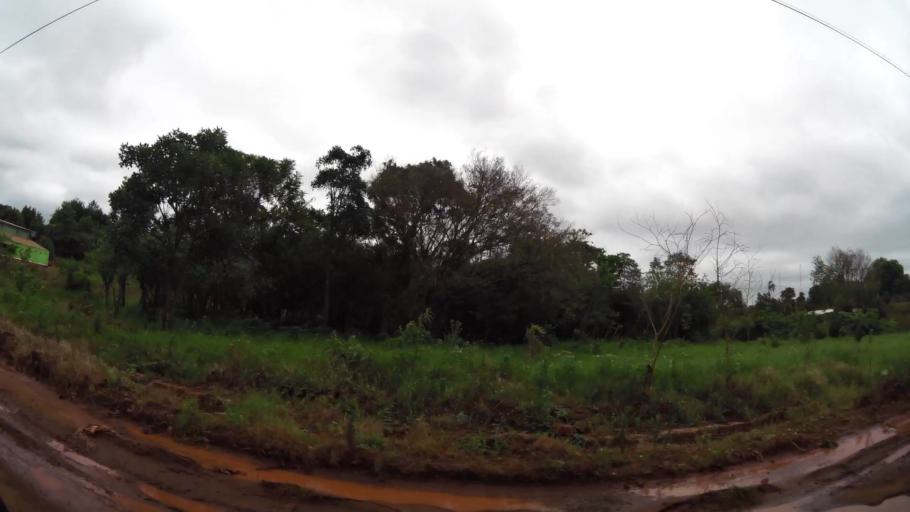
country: PY
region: Alto Parana
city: Ciudad del Este
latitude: -25.5002
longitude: -54.6878
